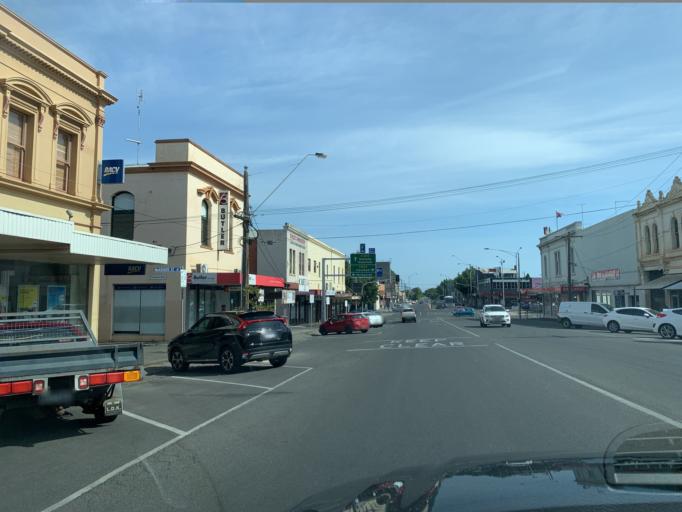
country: AU
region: Victoria
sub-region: Ballarat North
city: Ballarat Central
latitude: -37.5606
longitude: 143.8550
